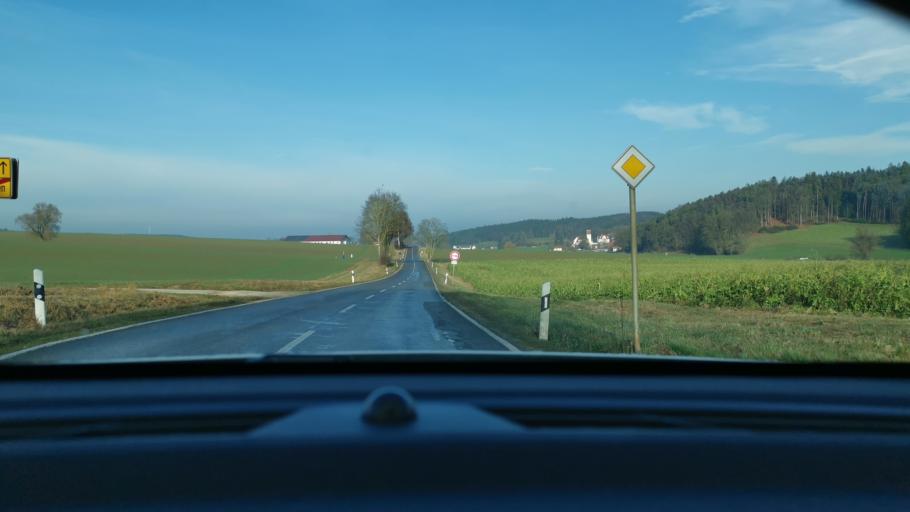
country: DE
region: Bavaria
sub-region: Swabia
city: Aindling
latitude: 48.5586
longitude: 10.9856
